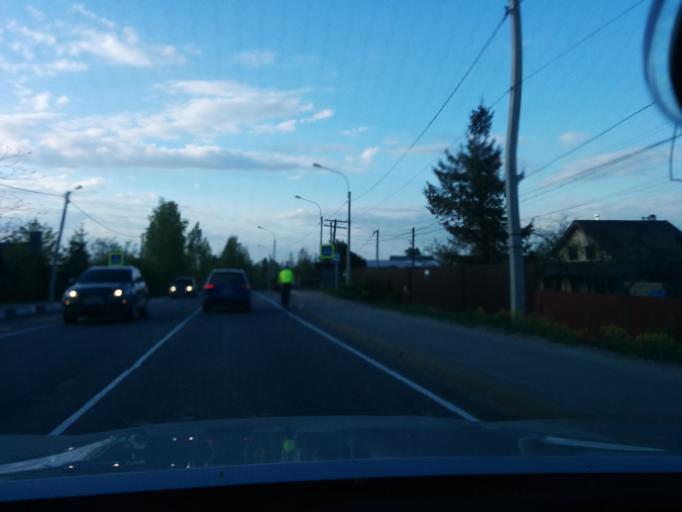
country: RU
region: Leningrad
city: Verkhniye Osel'ki
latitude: 60.2487
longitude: 30.4463
